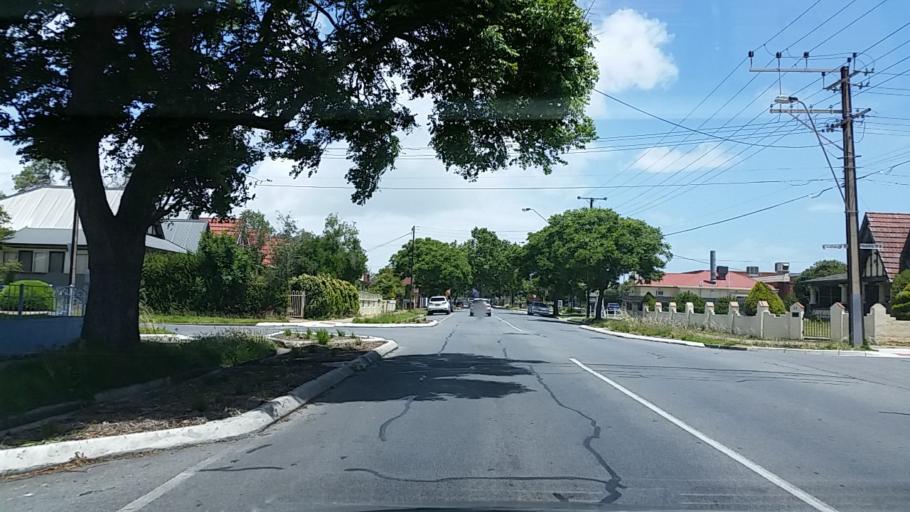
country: AU
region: South Australia
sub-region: Charles Sturt
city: Allenby Gardens
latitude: -34.8895
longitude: 138.5586
